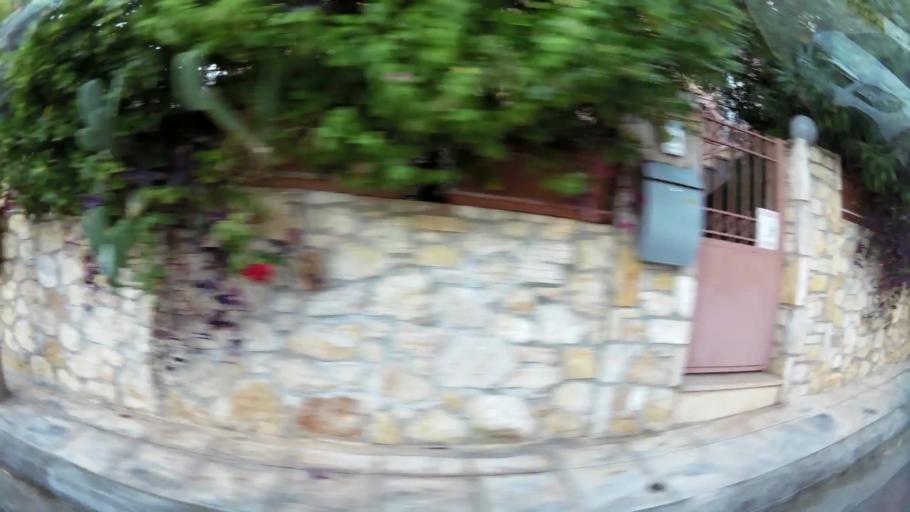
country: GR
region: Attica
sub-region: Nomarchia Anatolikis Attikis
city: Paiania
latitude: 37.9543
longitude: 23.8450
